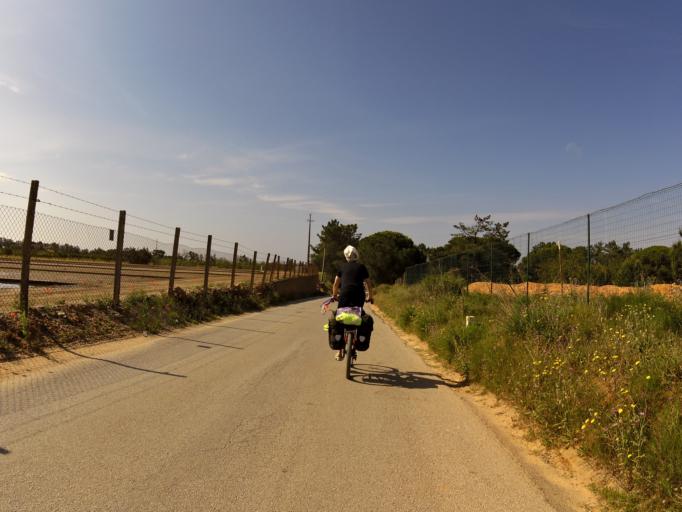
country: PT
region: Faro
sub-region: Loule
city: Almancil
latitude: 37.0657
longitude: -8.0149
